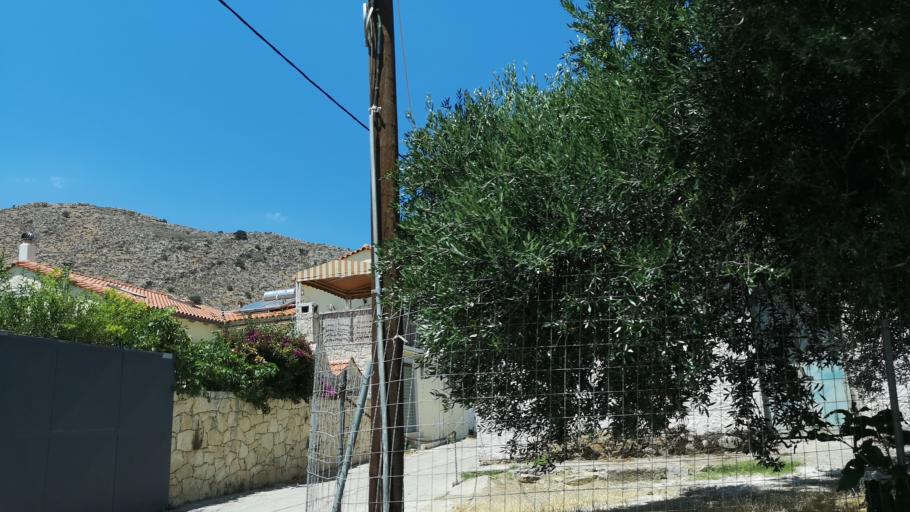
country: GR
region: Crete
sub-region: Nomos Lasithiou
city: Neapoli
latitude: 35.2464
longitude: 25.6380
